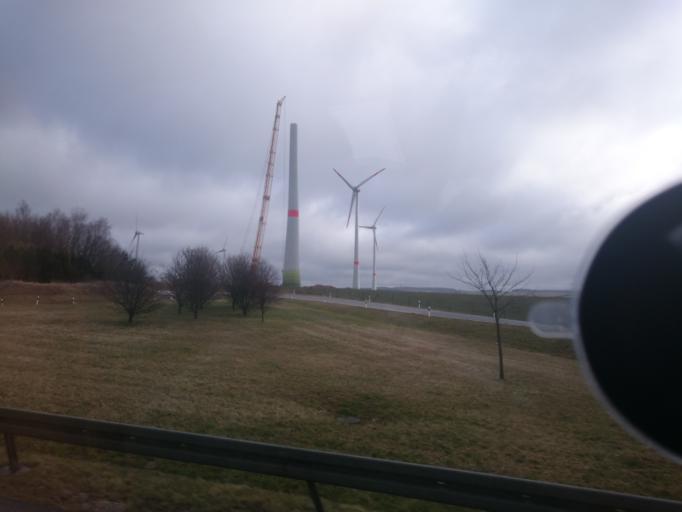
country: DE
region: Mecklenburg-Vorpommern
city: Muhl Rosin
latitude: 53.8252
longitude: 12.3005
